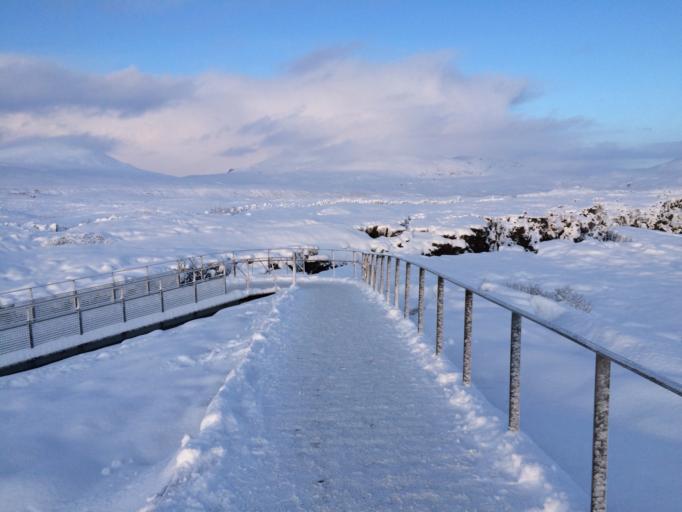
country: IS
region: South
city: Hveragerdi
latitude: 64.2556
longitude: -21.1281
